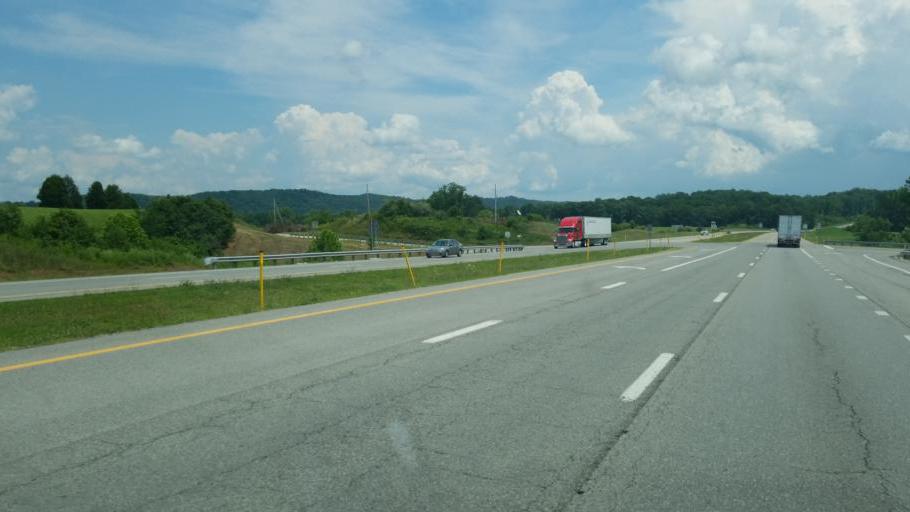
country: US
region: West Virginia
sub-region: Putnam County
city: Eleanor
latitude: 38.5491
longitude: -81.9815
